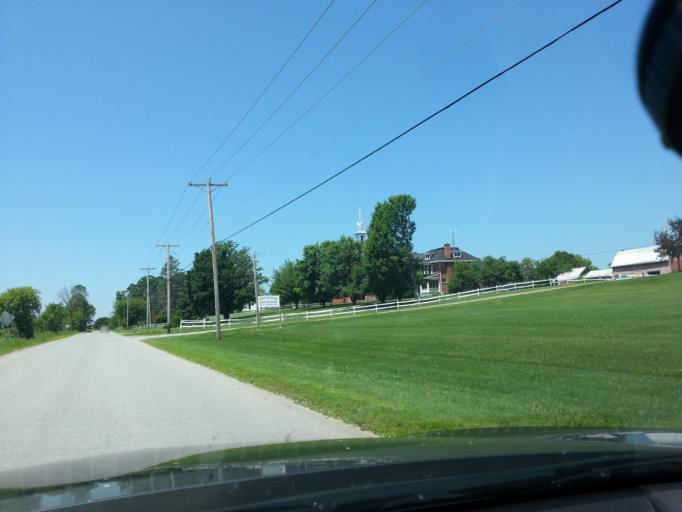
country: CA
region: Ontario
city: Arnprior
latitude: 45.5314
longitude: -76.3746
